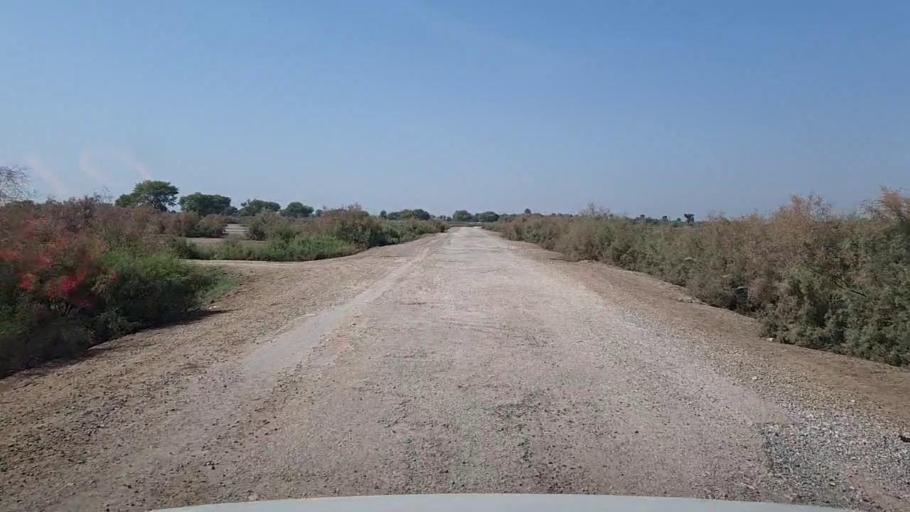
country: PK
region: Sindh
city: Kandhkot
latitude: 28.3358
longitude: 69.3650
